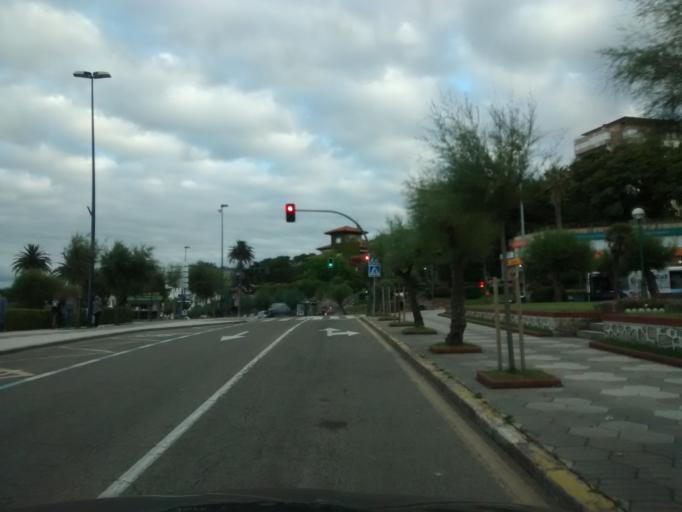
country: ES
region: Cantabria
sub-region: Provincia de Cantabria
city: Santander
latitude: 43.4744
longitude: -3.7853
